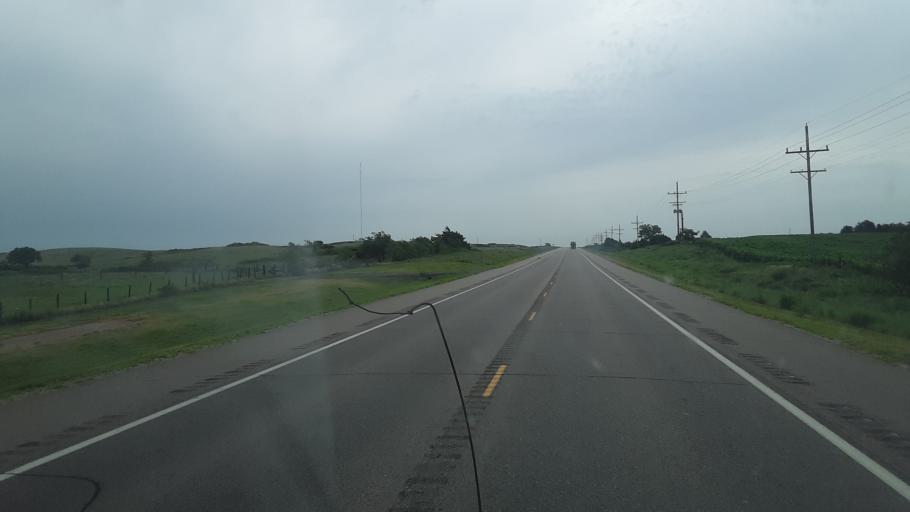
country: US
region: Kansas
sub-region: Edwards County
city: Kinsley
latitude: 37.9276
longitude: -99.3479
